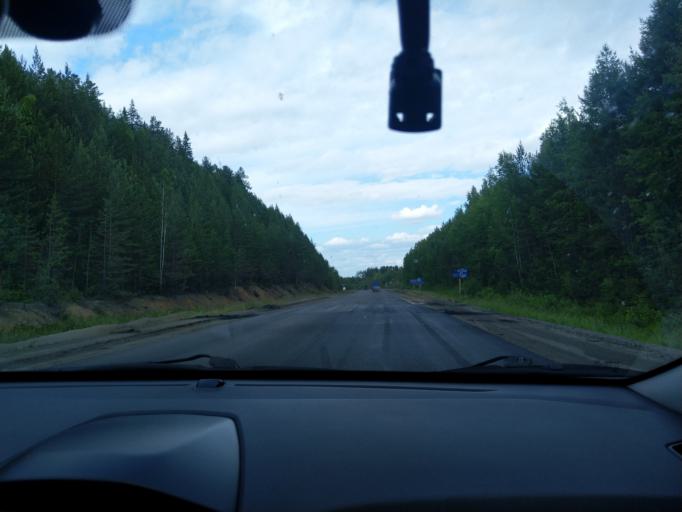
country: RU
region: Sverdlovsk
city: Nizhniy Tagil
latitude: 57.9208
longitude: 59.8468
